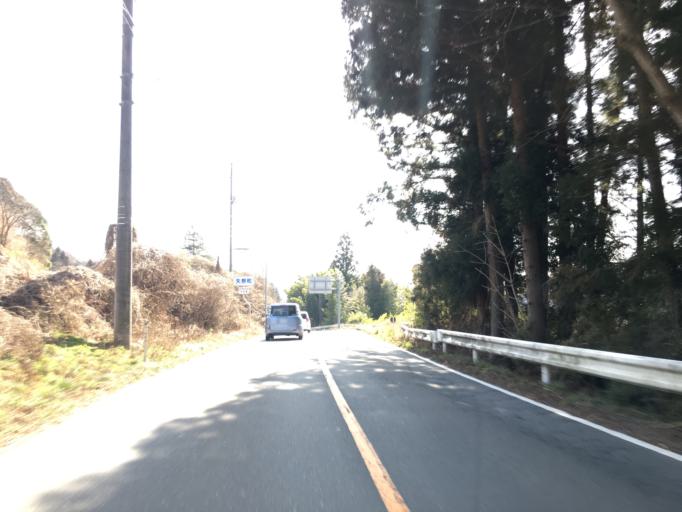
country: JP
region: Ibaraki
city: Daigo
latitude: 36.9320
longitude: 140.4152
